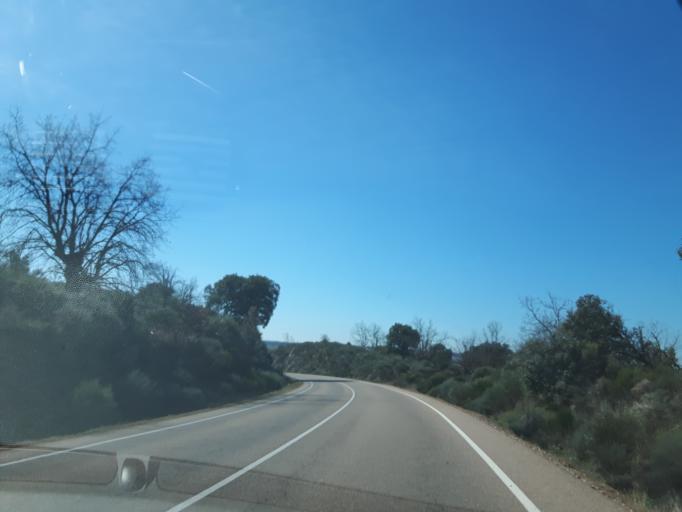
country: ES
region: Castille and Leon
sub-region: Provincia de Salamanca
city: Cerralbo
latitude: 40.9917
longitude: -6.5568
